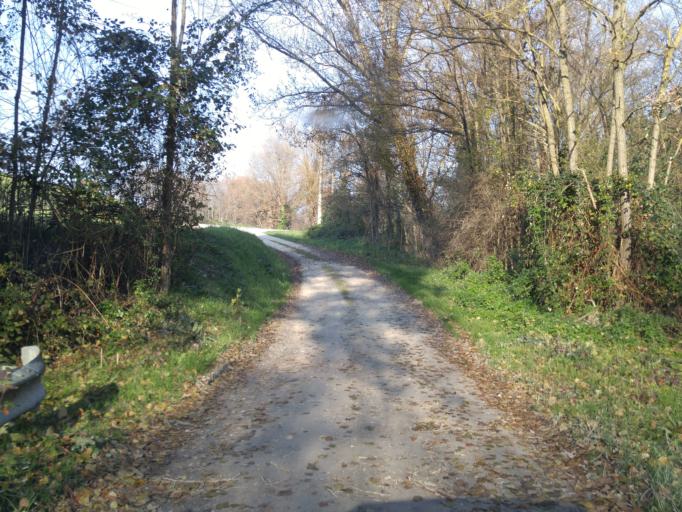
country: IT
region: The Marches
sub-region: Provincia di Pesaro e Urbino
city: Tavernelle
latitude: 43.7106
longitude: 12.8897
